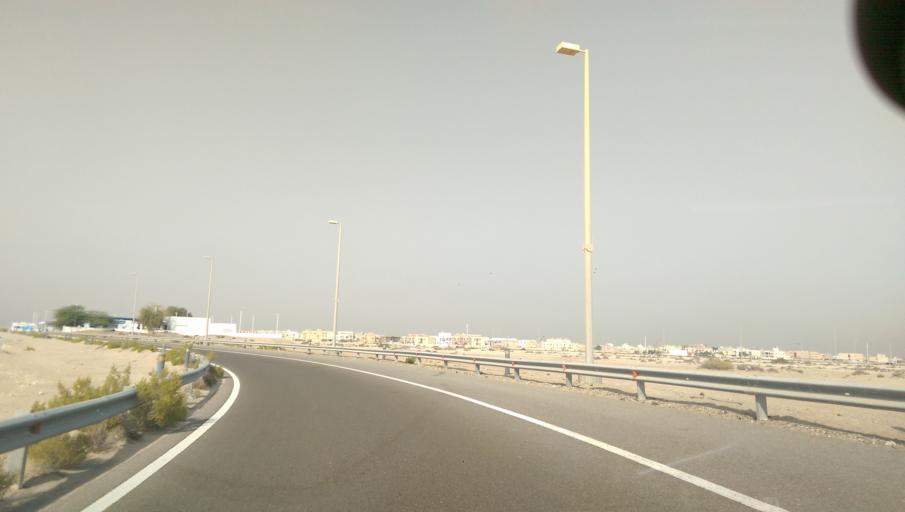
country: AE
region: Abu Dhabi
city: Abu Dhabi
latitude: 24.3572
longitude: 54.6464
